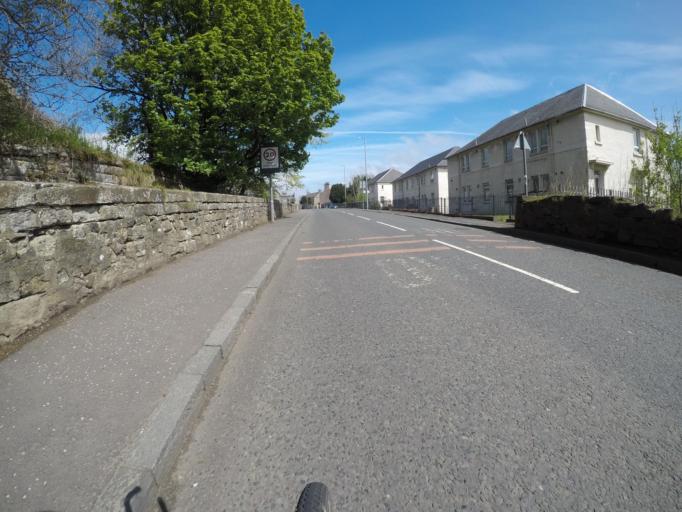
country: GB
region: Scotland
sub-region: East Ayrshire
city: Stewarton
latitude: 55.6781
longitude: -4.5195
